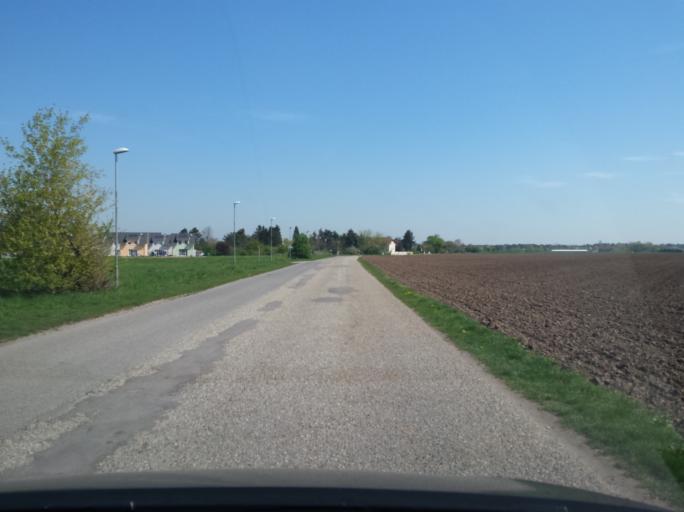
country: AT
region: Lower Austria
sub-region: Politischer Bezirk Ganserndorf
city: Parbasdorf
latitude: 48.3119
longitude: 16.5980
